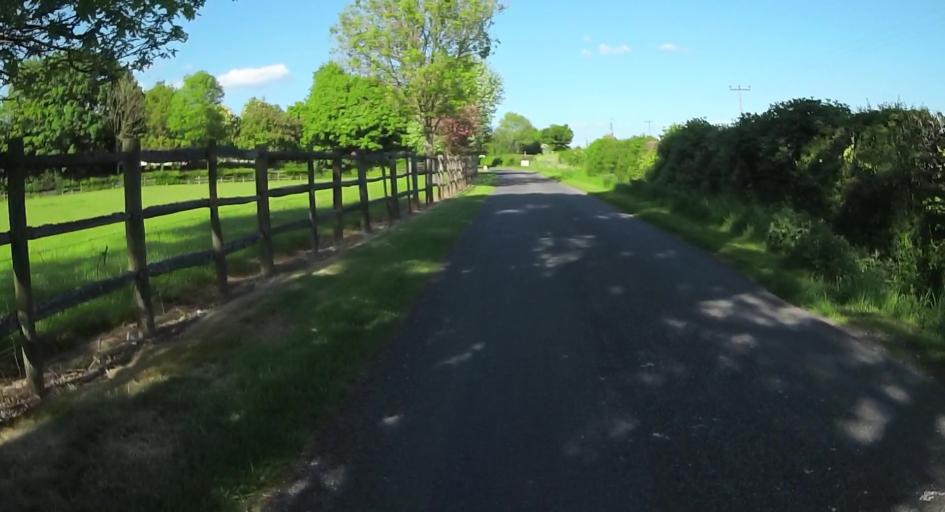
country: GB
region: England
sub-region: Hampshire
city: Overton
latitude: 51.1758
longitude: -1.2057
